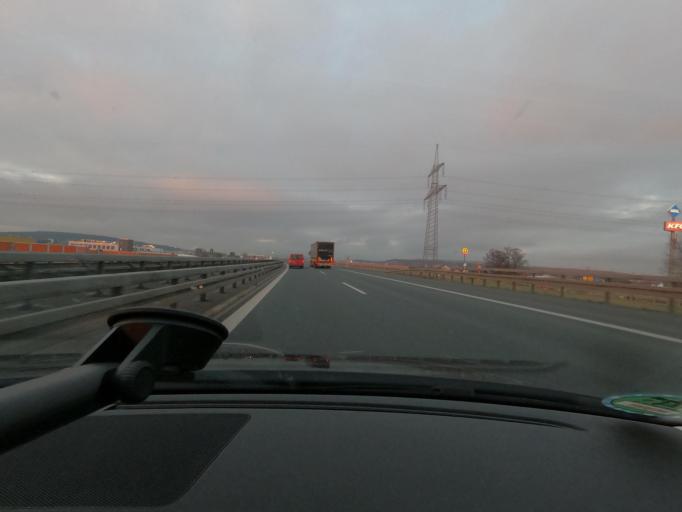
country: DE
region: Bavaria
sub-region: Upper Franconia
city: Forchheim
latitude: 49.6972
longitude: 11.0623
